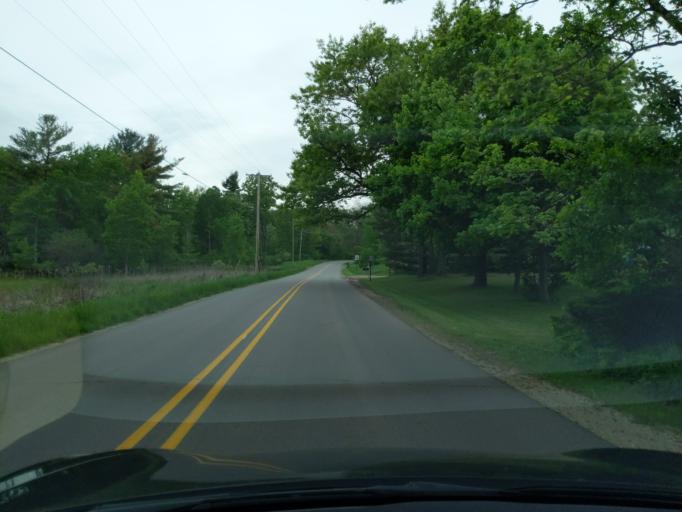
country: US
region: Michigan
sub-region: Ingham County
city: Leslie
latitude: 42.3910
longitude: -84.3541
